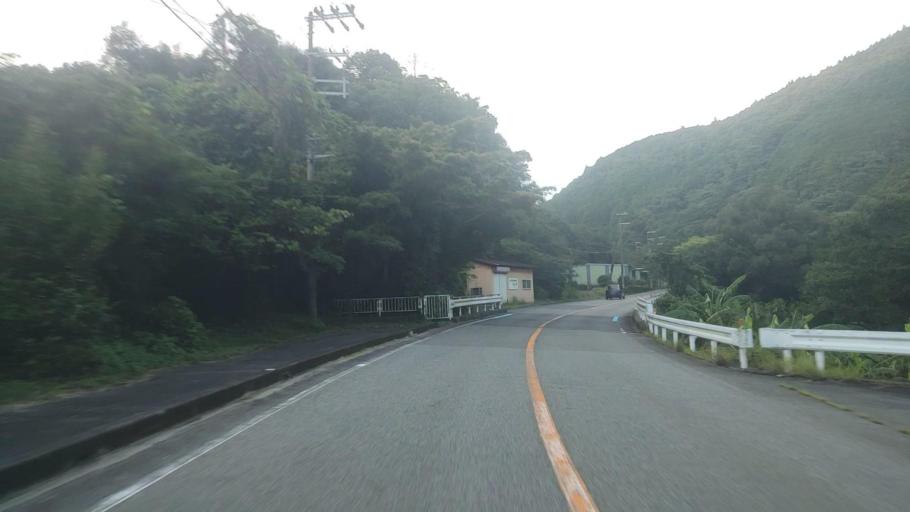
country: JP
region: Wakayama
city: Tanabe
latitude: 33.8139
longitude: 135.5512
